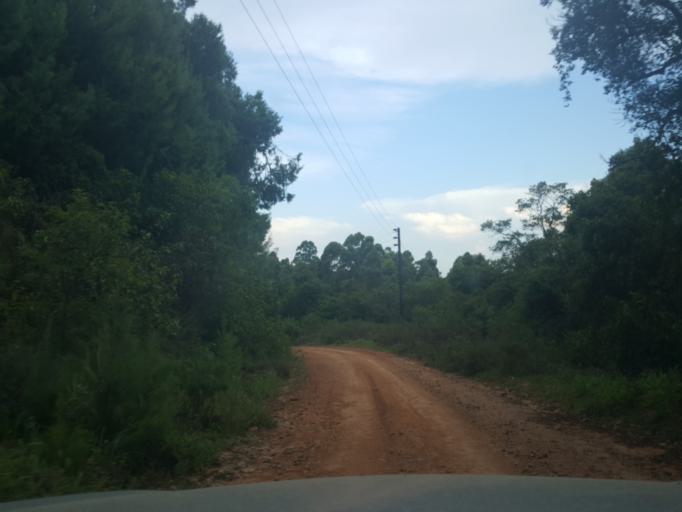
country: ZA
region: Limpopo
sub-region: Mopani District Municipality
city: Hoedspruit
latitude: -24.5843
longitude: 30.8654
